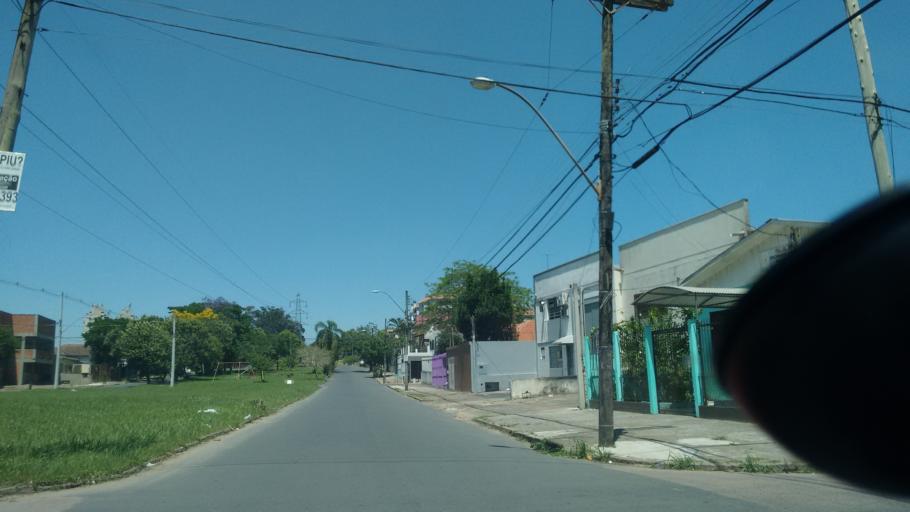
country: BR
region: Rio Grande do Sul
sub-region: Cachoeirinha
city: Cachoeirinha
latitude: -29.9994
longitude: -51.1266
